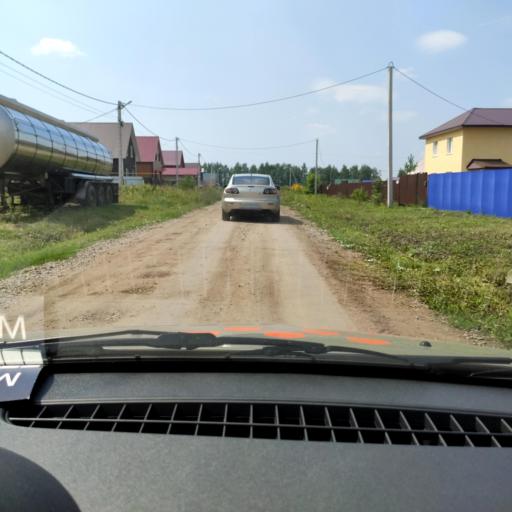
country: RU
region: Bashkortostan
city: Iglino
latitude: 54.8303
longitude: 56.4469
